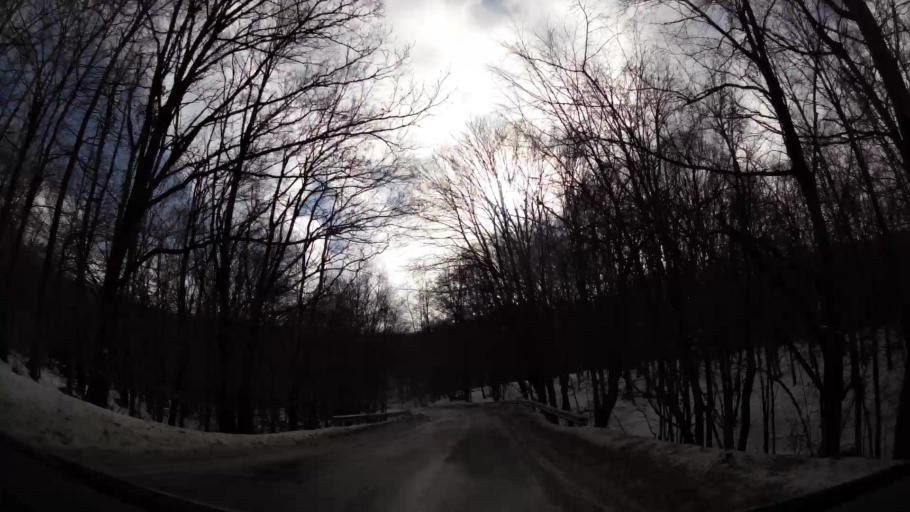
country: BG
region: Sofia-Capital
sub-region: Stolichna Obshtina
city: Sofia
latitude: 42.6328
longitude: 23.2245
